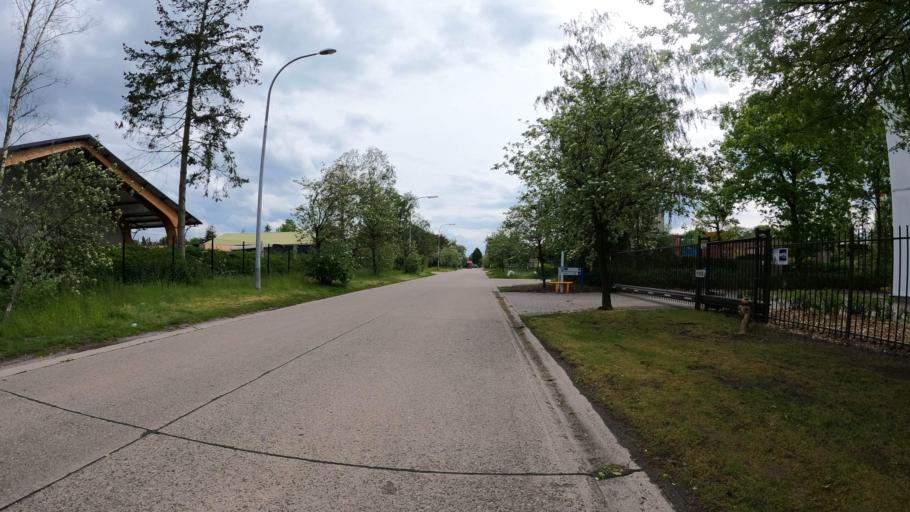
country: BE
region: Flanders
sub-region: Provincie Antwerpen
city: Vosselaar
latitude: 51.2898
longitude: 4.9149
